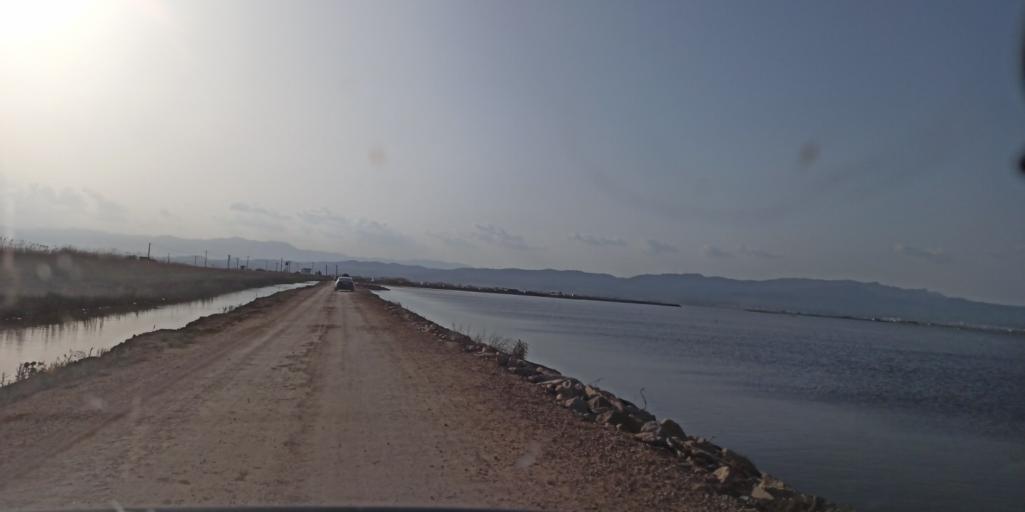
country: ES
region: Catalonia
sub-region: Provincia de Tarragona
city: L'Ampolla
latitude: 40.7653
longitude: 0.7446
